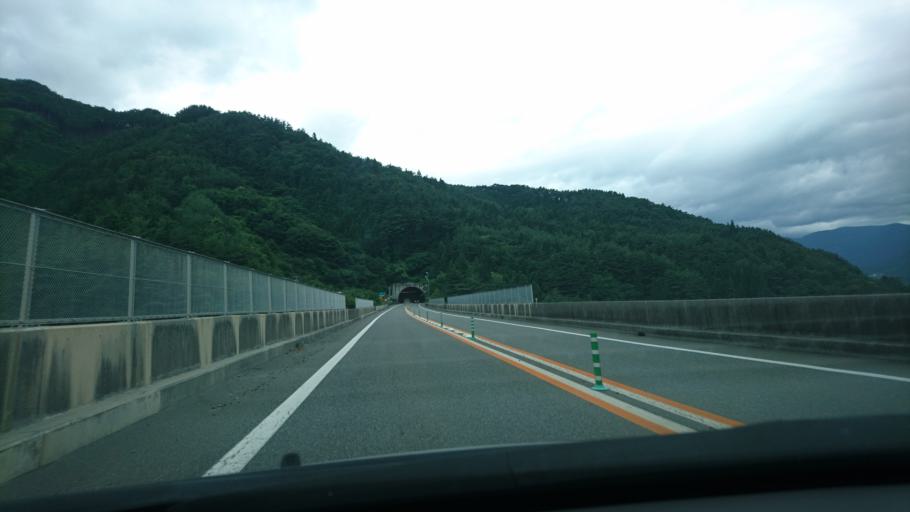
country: JP
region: Iwate
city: Ofunato
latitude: 39.0593
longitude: 141.7105
